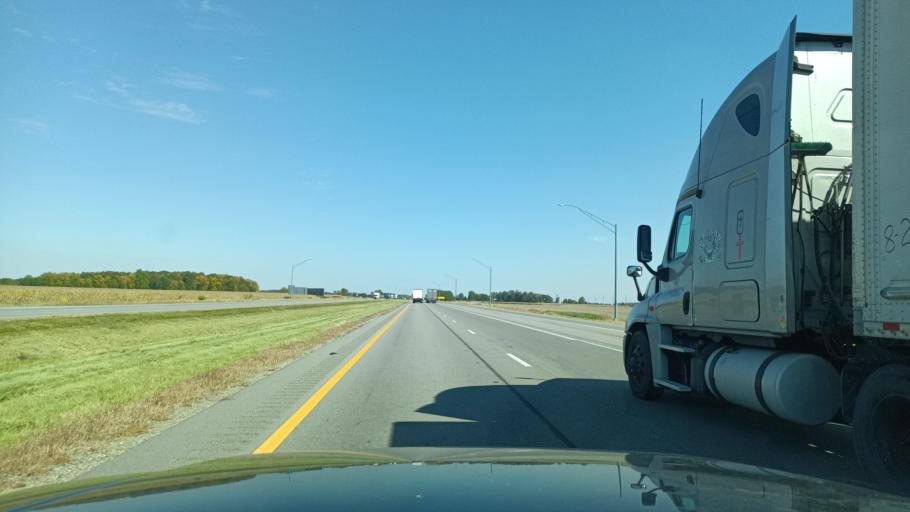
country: US
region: Ohio
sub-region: Defiance County
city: Defiance
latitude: 41.3134
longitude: -84.3204
